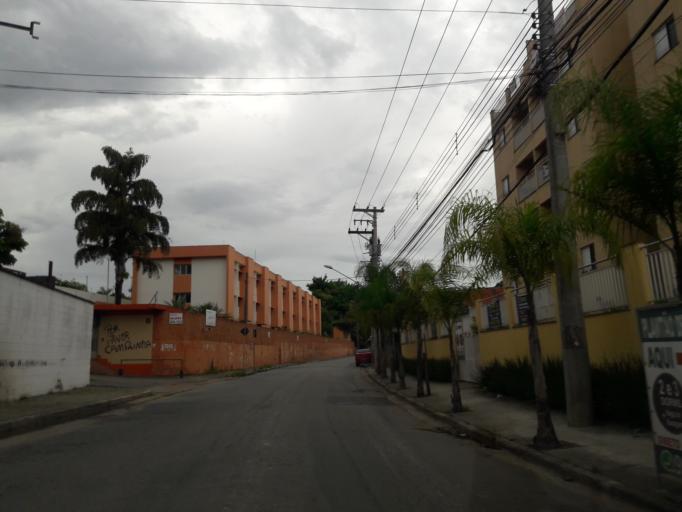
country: BR
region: Sao Paulo
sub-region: Itaquaquecetuba
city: Itaquaquecetuba
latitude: -23.4222
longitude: -46.3974
